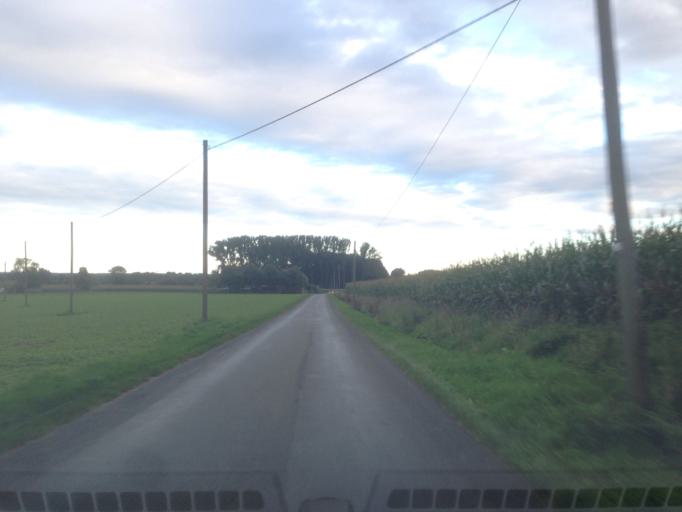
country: DE
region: North Rhine-Westphalia
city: Olfen
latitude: 51.7342
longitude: 7.3704
